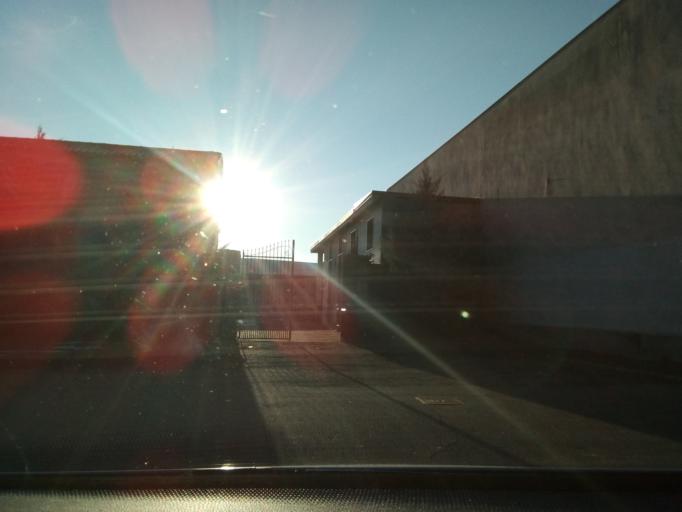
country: IT
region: Piedmont
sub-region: Provincia di Torino
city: Burolo
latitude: 45.4763
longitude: 7.9356
